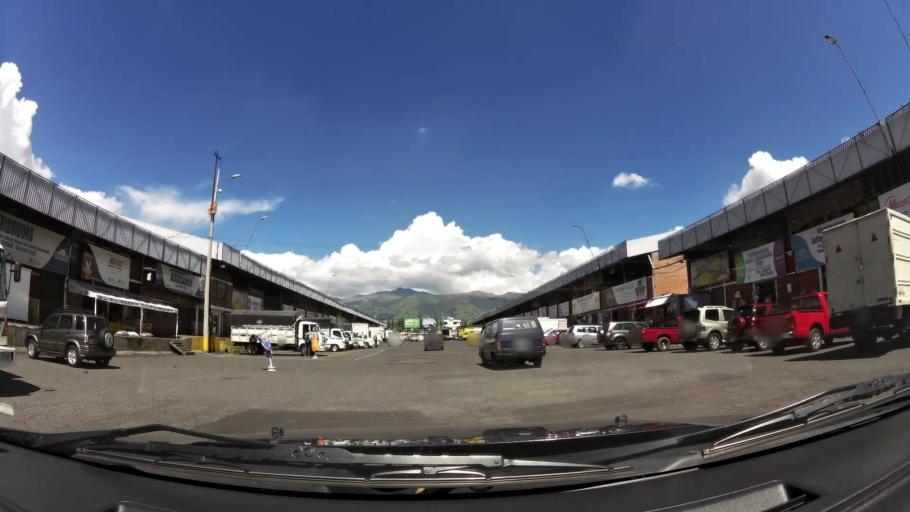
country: EC
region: Pichincha
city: Quito
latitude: -0.2706
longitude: -78.5351
